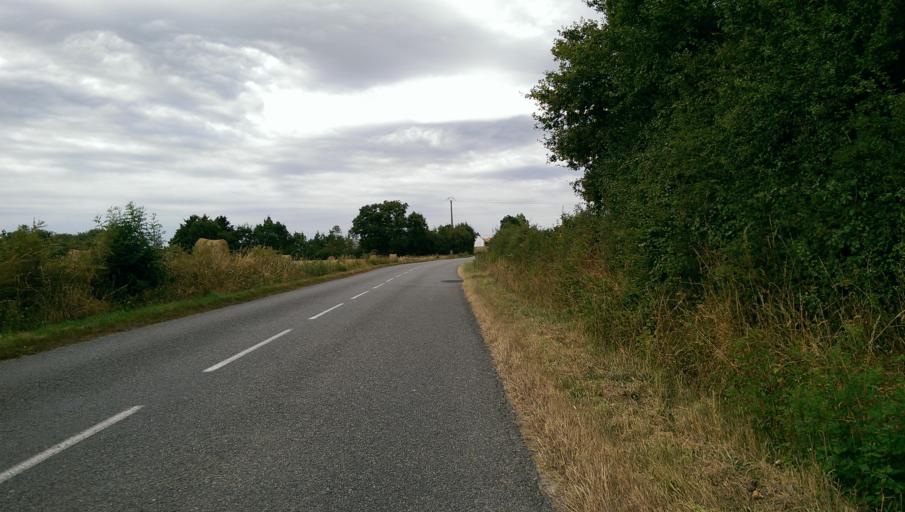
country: FR
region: Pays de la Loire
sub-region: Departement de la Loire-Atlantique
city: Vieillevigne
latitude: 46.9800
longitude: -1.4308
